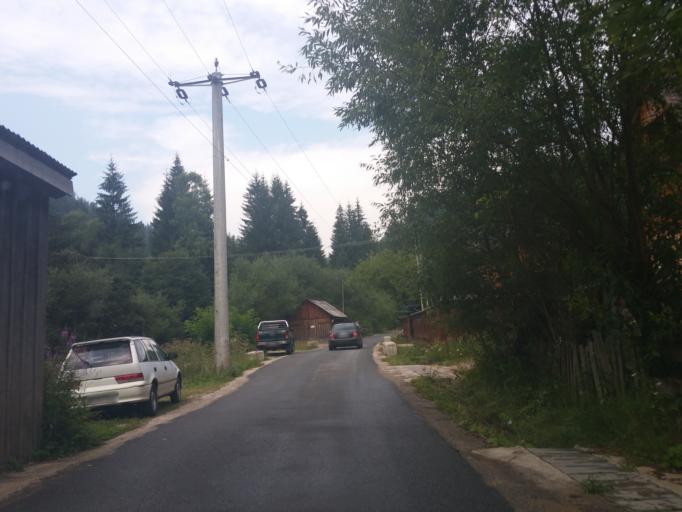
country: RO
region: Alba
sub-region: Comuna Garda de Sus
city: Garda de Sus
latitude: 46.4678
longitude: 22.8206
